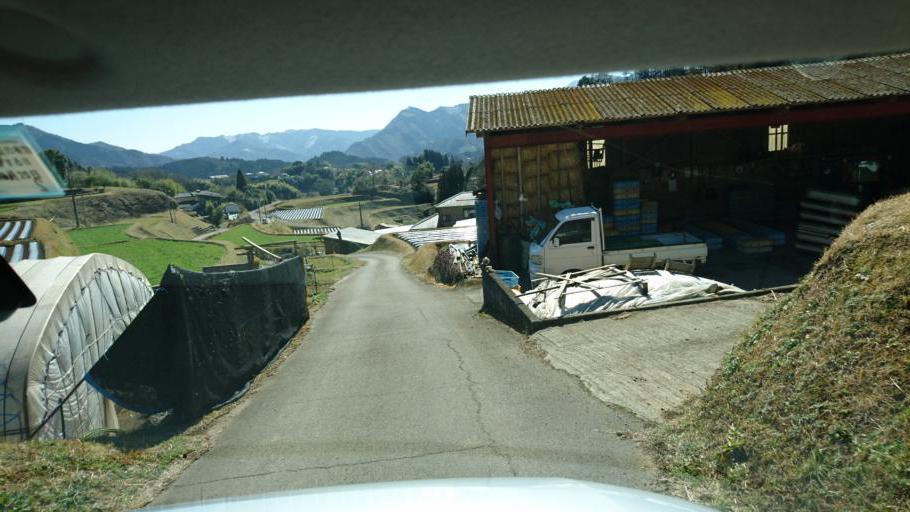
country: JP
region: Oita
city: Takedamachi
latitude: 32.7262
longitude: 131.3075
